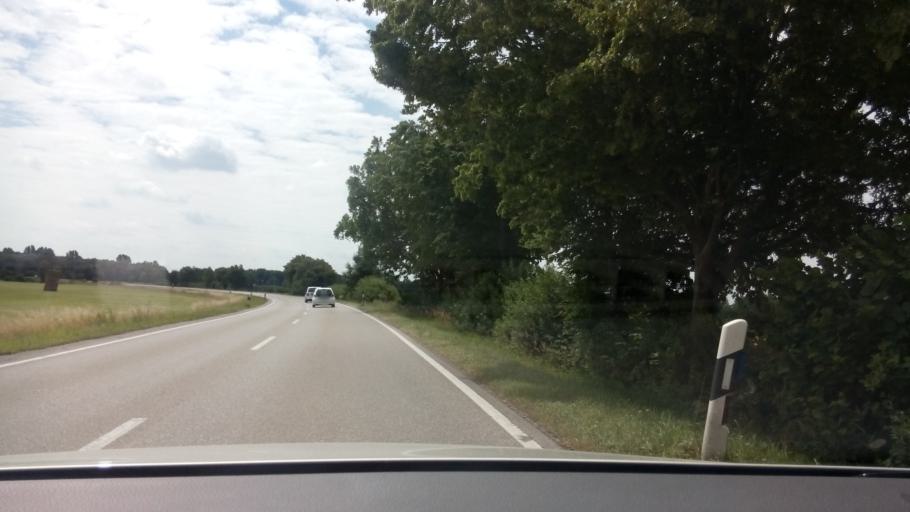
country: DE
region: Bavaria
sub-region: Upper Bavaria
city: Marzling
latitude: 48.3789
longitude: 11.7833
